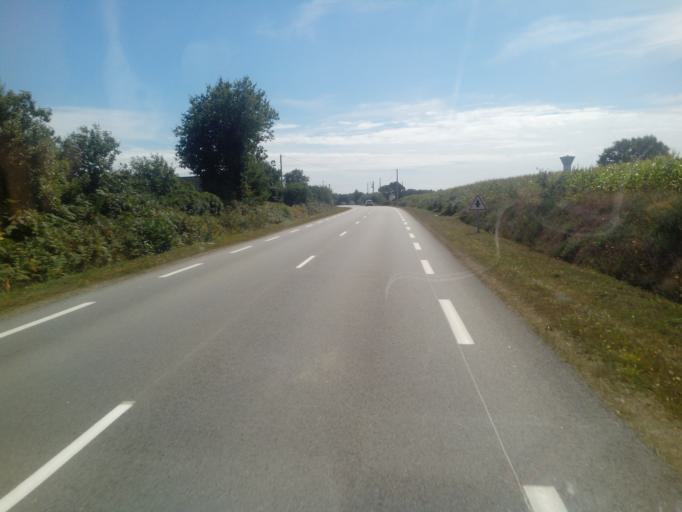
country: FR
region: Brittany
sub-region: Departement du Morbihan
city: Peaule
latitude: 47.5484
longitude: -2.3976
